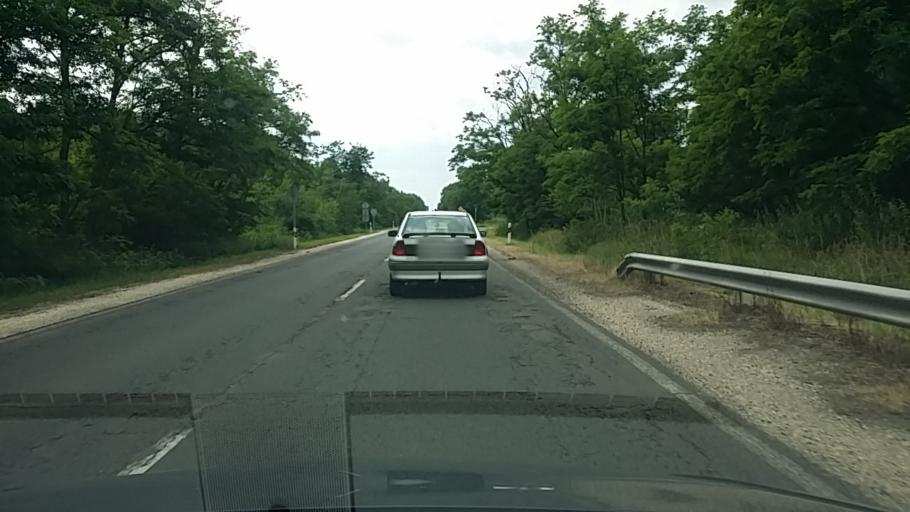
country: HU
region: Pest
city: Hernad
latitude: 47.1640
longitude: 19.3795
